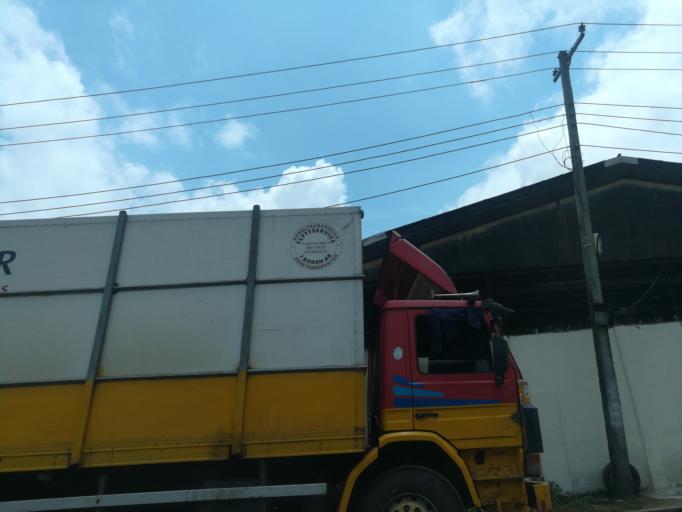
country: NG
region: Lagos
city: Oshodi
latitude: 6.5555
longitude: 3.3578
